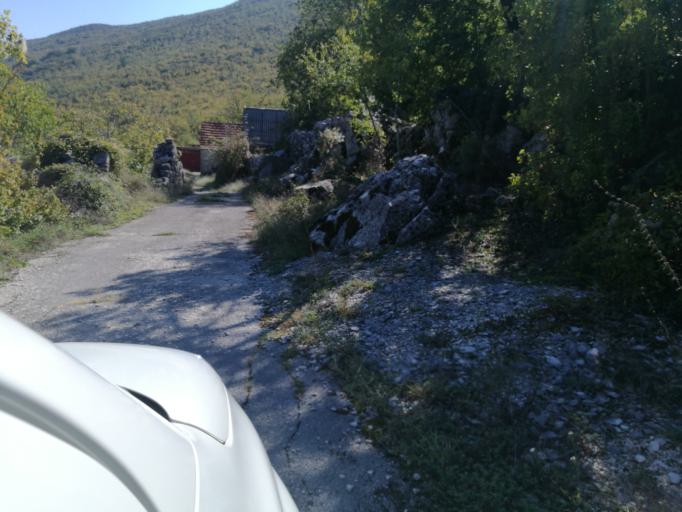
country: HR
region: Splitsko-Dalmatinska
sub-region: Grad Omis
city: Omis
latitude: 43.5130
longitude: 16.7331
